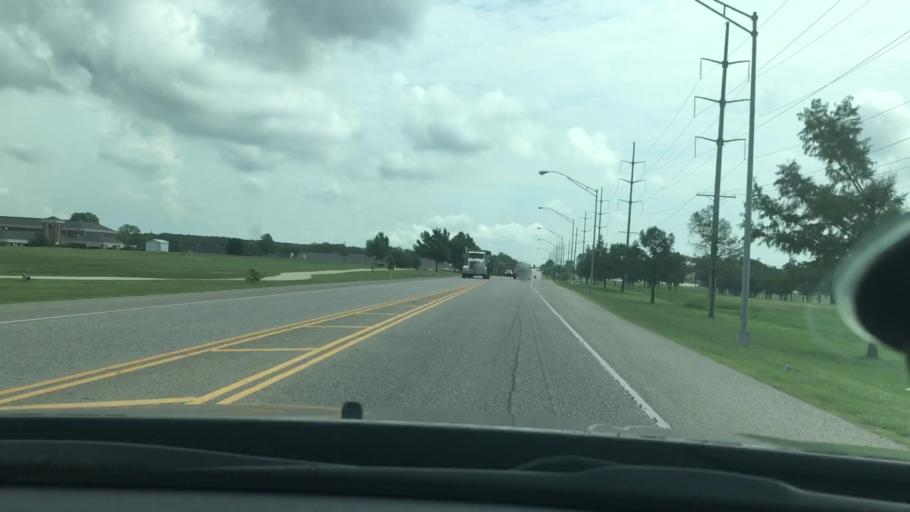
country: US
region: Oklahoma
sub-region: Carter County
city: Ardmore
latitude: 34.2028
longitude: -97.1293
